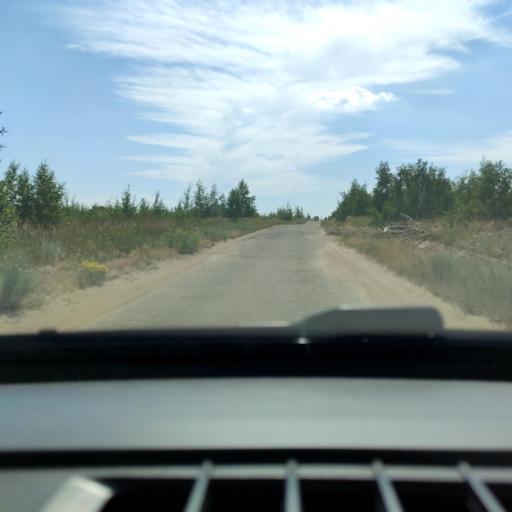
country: RU
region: Voronezj
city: Somovo
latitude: 51.7705
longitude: 39.3356
